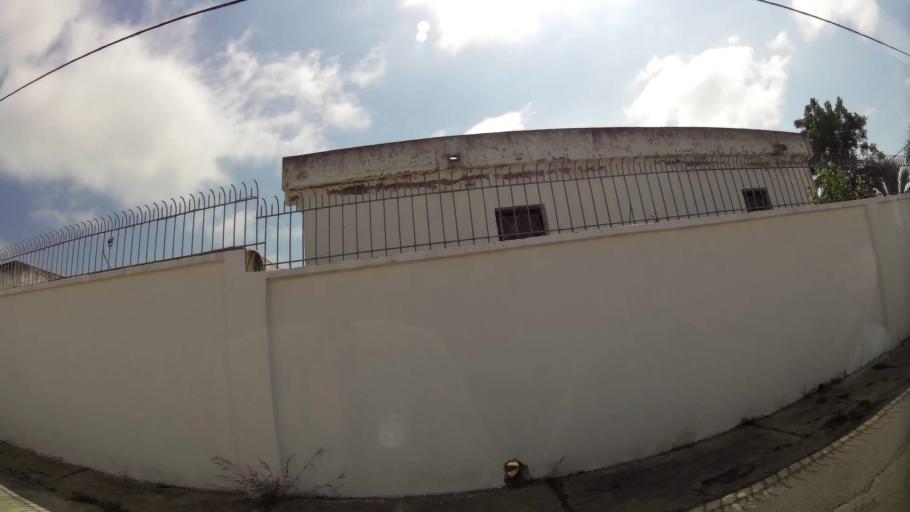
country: MA
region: Rabat-Sale-Zemmour-Zaer
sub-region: Rabat
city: Rabat
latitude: 33.9800
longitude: -6.8406
